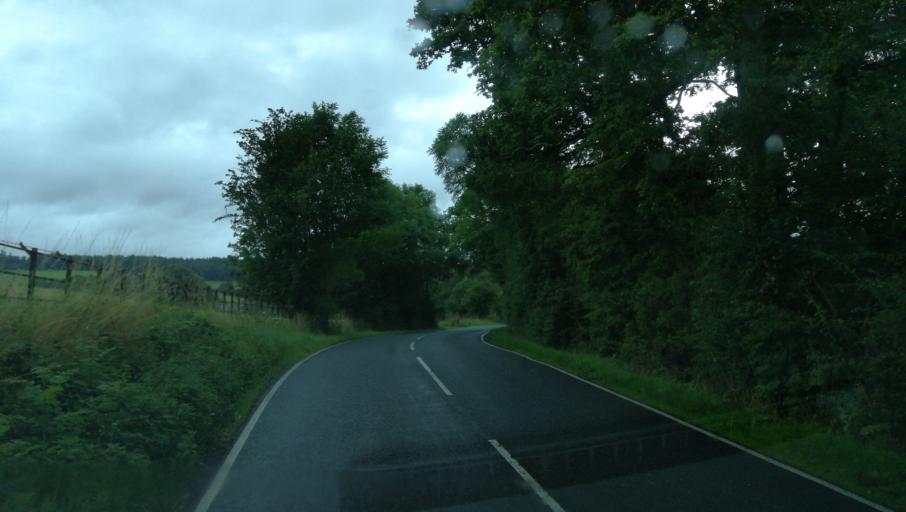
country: GB
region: England
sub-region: Cumbria
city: Penrith
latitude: 54.6273
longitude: -2.8123
